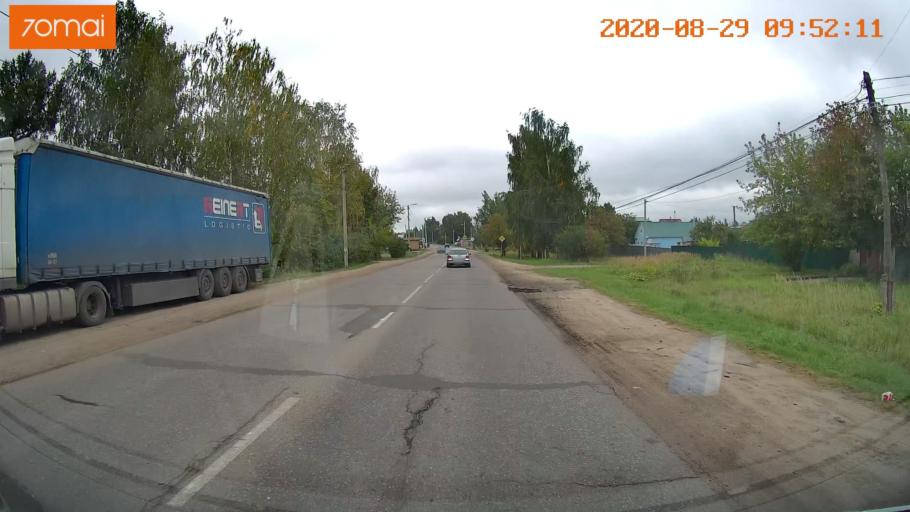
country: RU
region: Ivanovo
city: Kineshma
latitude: 57.4248
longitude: 42.2063
